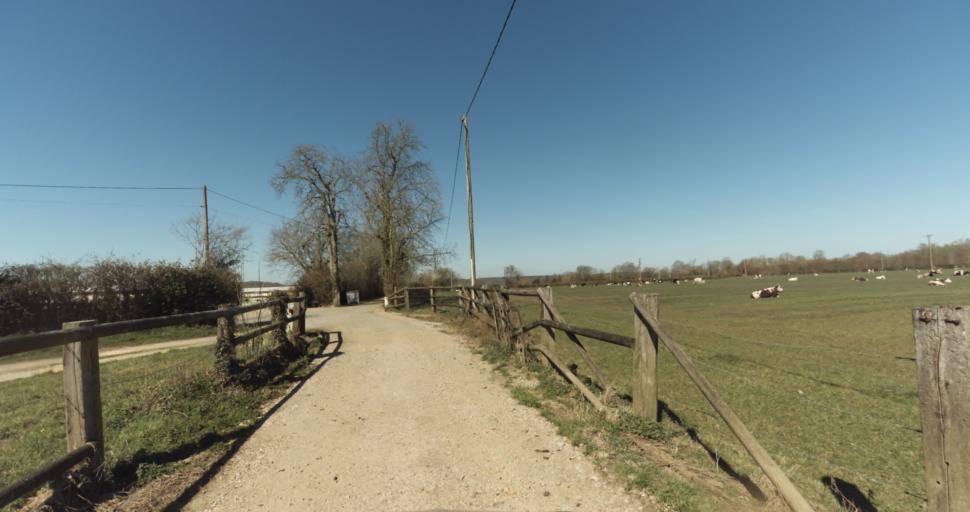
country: FR
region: Lower Normandy
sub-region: Departement du Calvados
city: Livarot
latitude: 48.9789
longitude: 0.0874
